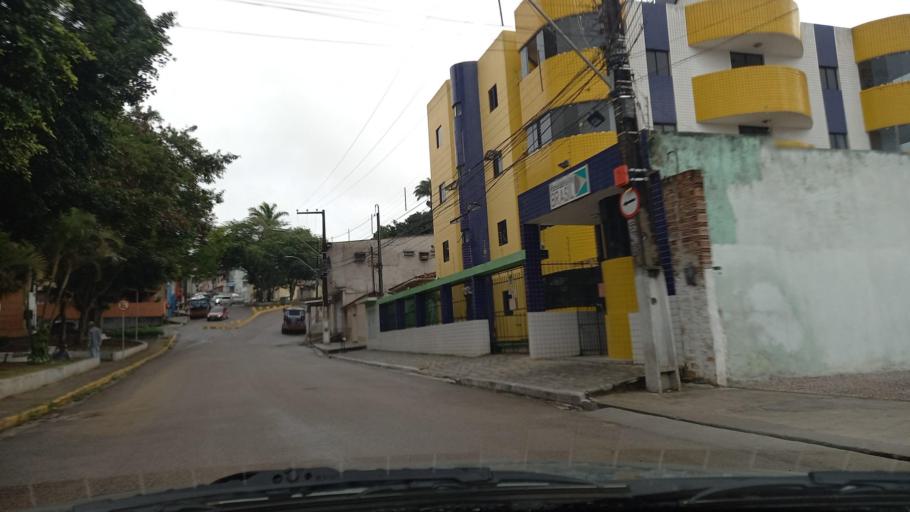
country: BR
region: Pernambuco
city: Garanhuns
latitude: -8.8948
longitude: -36.4911
